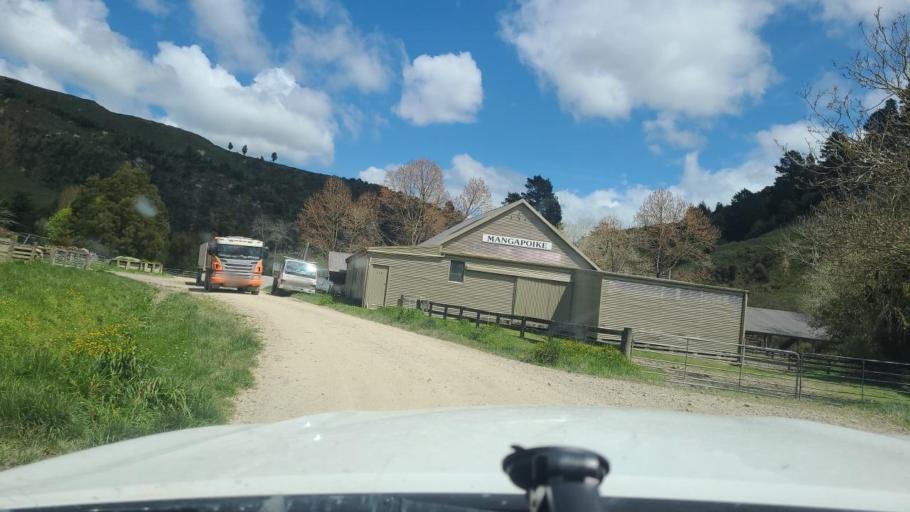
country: NZ
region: Hawke's Bay
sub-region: Wairoa District
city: Wairoa
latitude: -38.8478
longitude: 177.6802
